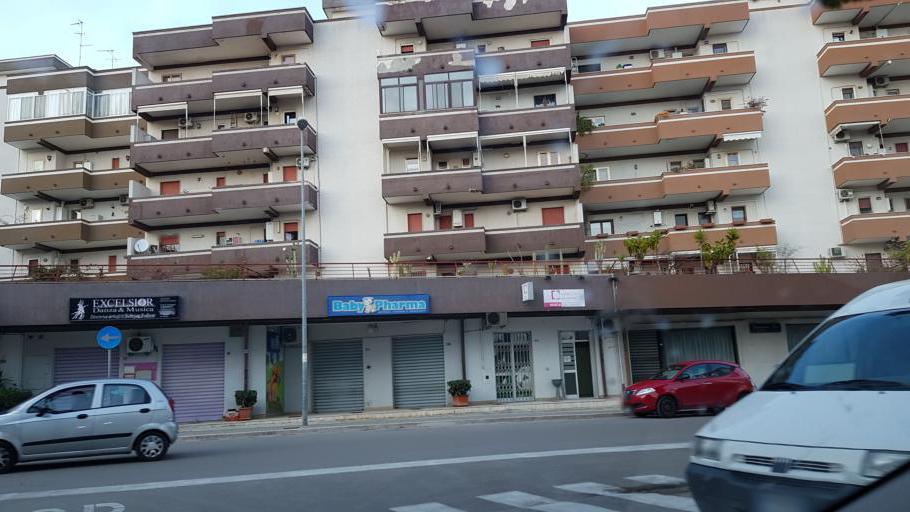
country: IT
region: Apulia
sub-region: Provincia di Brindisi
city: Brindisi
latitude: 40.6365
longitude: 17.9328
